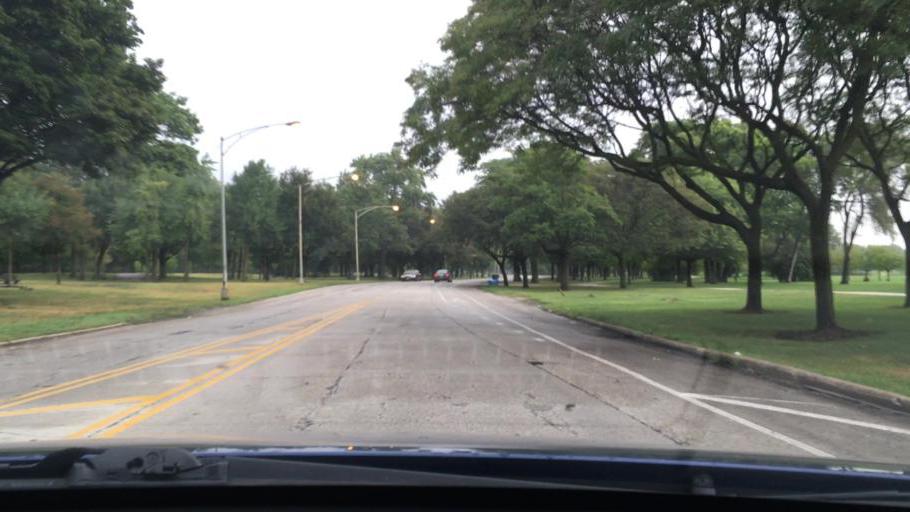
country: US
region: Illinois
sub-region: Cook County
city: Chicago
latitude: 41.7964
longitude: -87.6153
